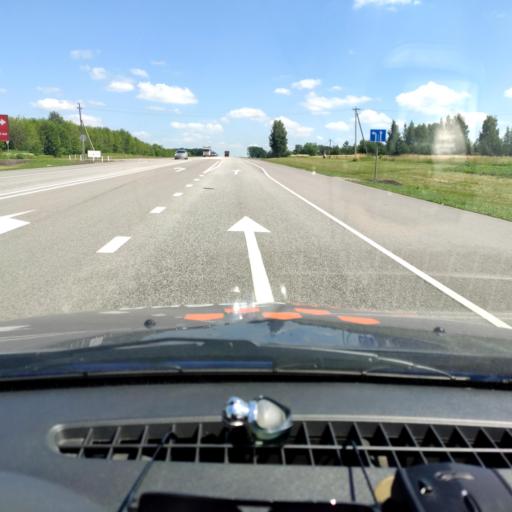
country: RU
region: Orjol
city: Orel
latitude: 52.8525
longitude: 36.2316
